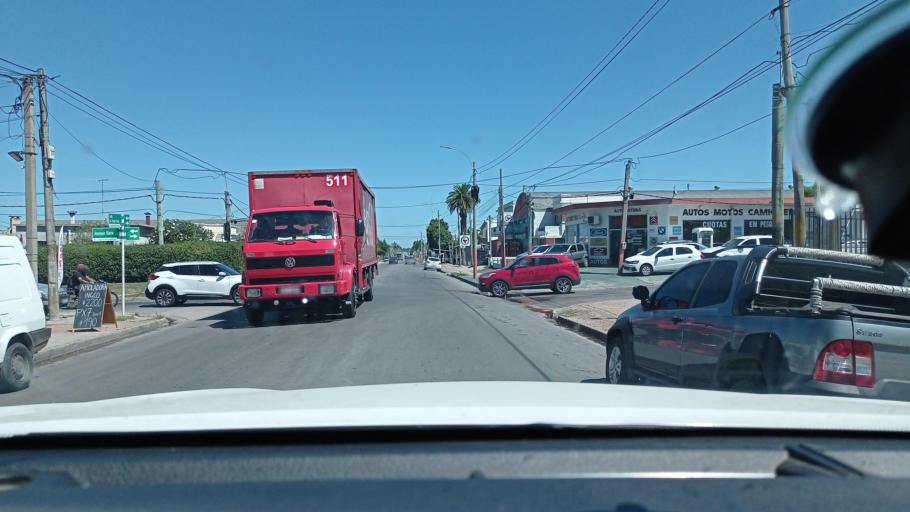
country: UY
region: Canelones
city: Las Piedras
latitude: -34.7362
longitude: -56.2238
